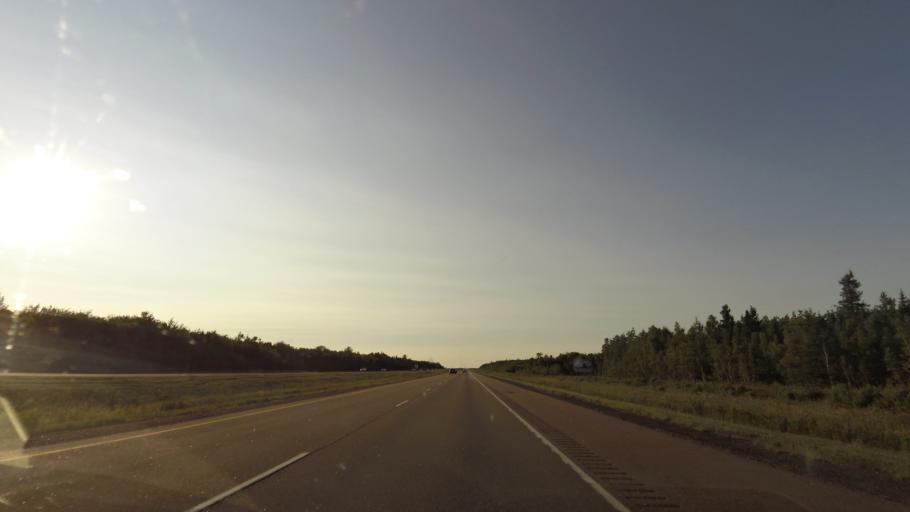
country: CA
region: New Brunswick
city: Dieppe
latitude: 46.1140
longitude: -64.6187
